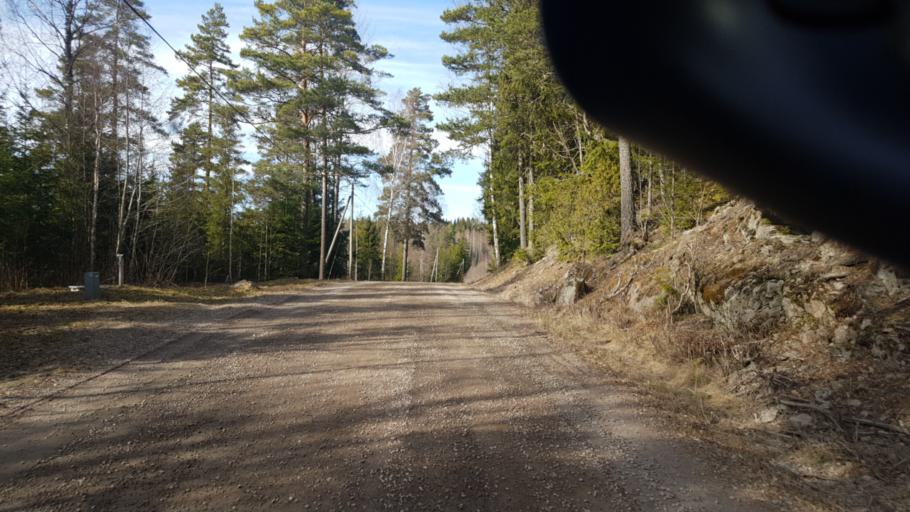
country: SE
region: Vaermland
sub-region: Eda Kommun
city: Amotfors
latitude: 59.7884
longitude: 12.3756
